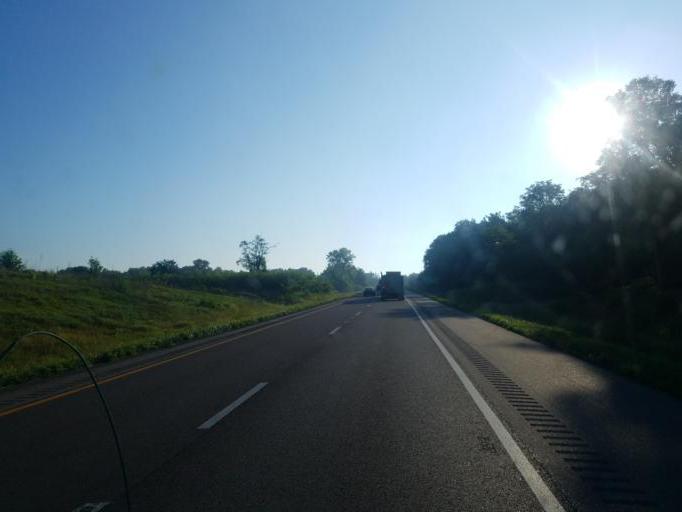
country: US
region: Illinois
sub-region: Bond County
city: Greenville
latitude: 38.9050
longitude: -89.2931
